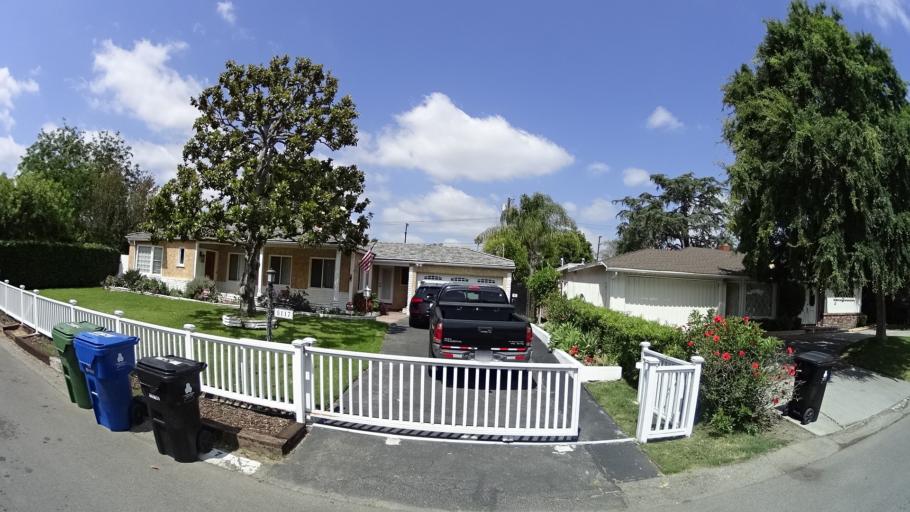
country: US
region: California
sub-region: Los Angeles County
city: North Hollywood
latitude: 34.1638
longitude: -118.3594
